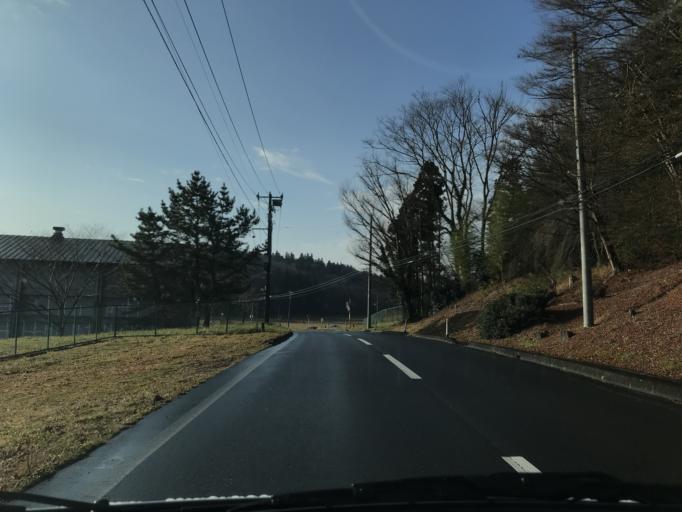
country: JP
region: Iwate
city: Ichinoseki
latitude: 38.7936
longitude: 141.1718
